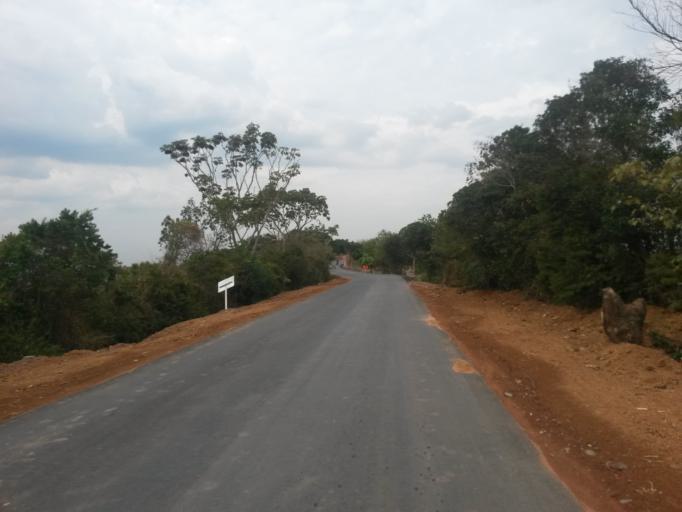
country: CO
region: Cauca
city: Buenos Aires
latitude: 3.0658
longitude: -76.6209
